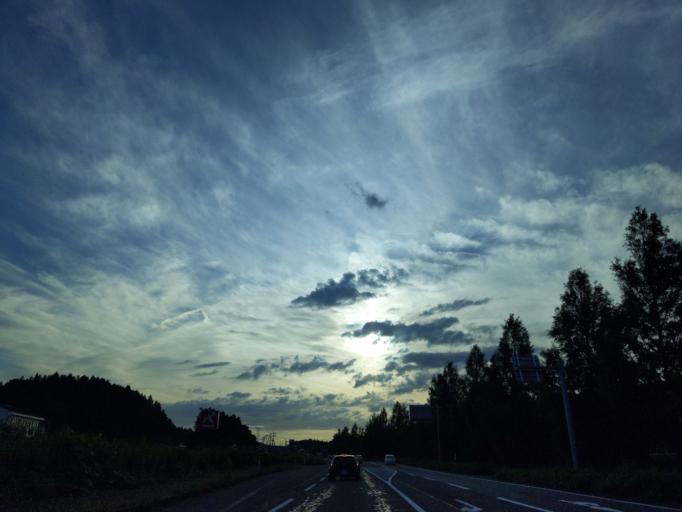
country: JP
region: Niigata
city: Kashiwazaki
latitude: 37.4533
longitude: 138.6551
